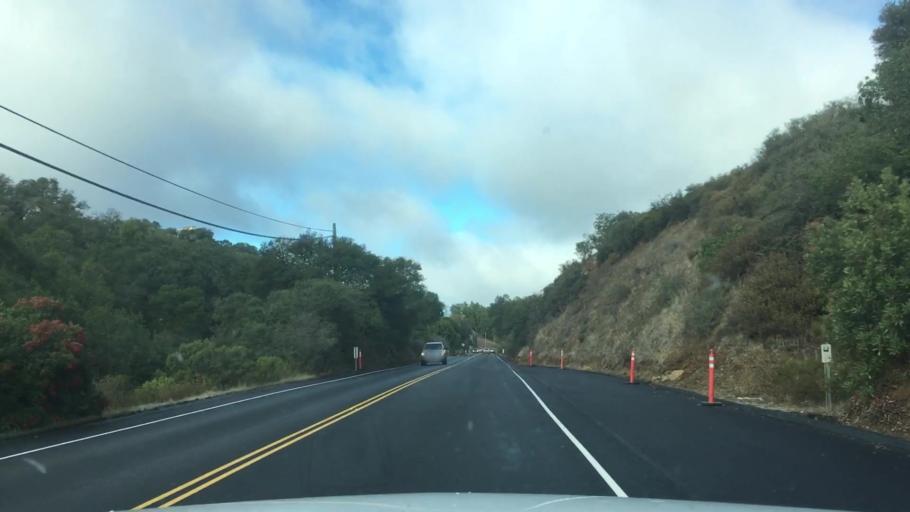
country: US
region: California
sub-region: San Luis Obispo County
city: Atascadero
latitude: 35.4530
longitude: -120.7106
